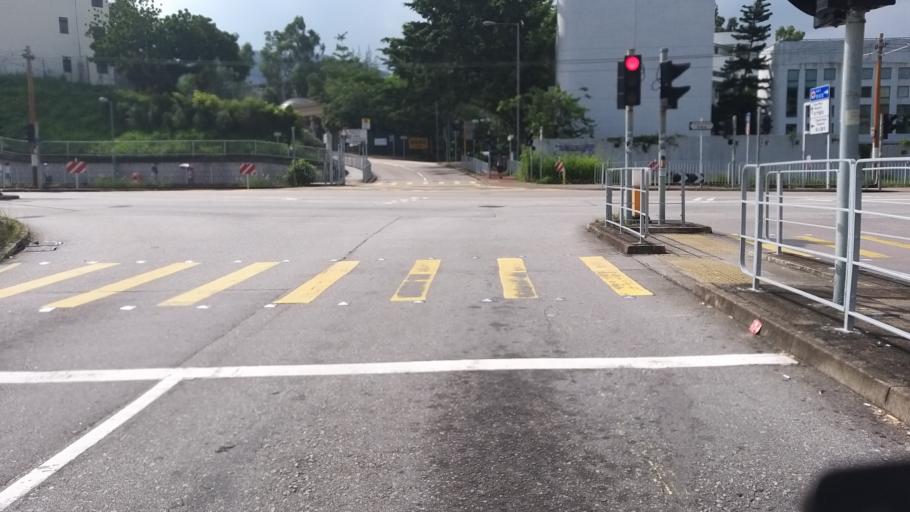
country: HK
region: Tuen Mun
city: Tuen Mun
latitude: 22.4076
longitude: 113.9745
